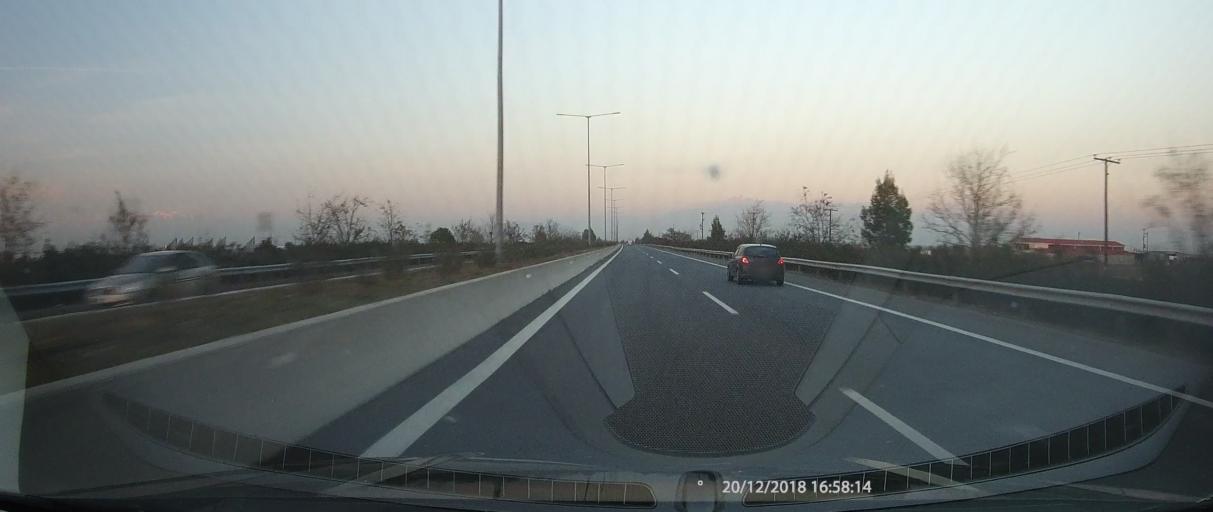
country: GR
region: Thessaly
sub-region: Nomos Larisis
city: Nikaia
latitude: 39.5908
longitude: 22.4891
